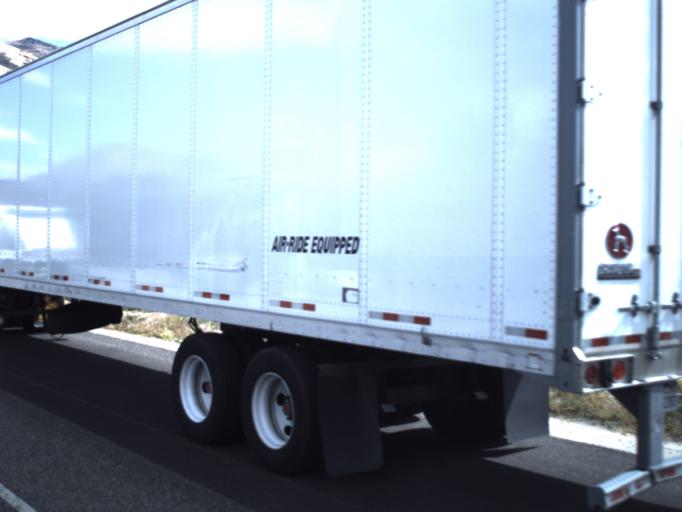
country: US
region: Utah
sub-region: Box Elder County
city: Perry
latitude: 41.4865
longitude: -112.0313
